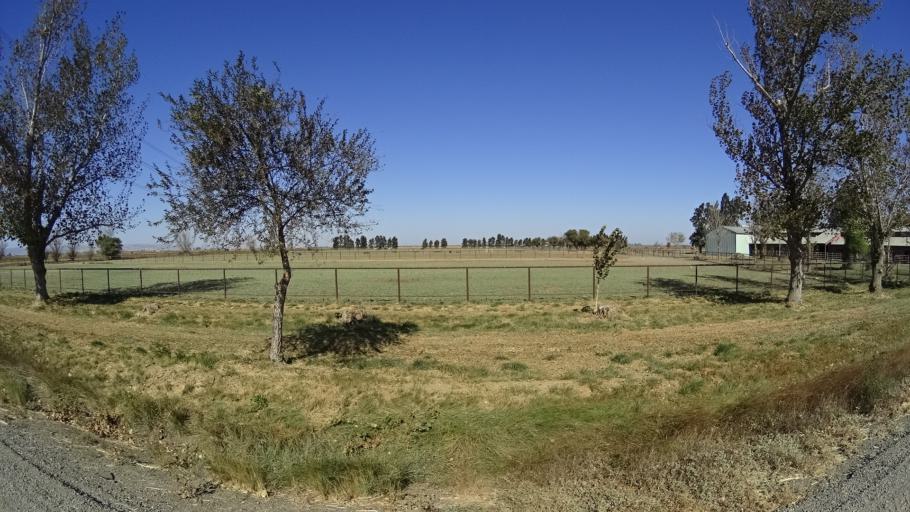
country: US
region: California
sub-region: Yolo County
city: Cottonwood
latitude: 38.6202
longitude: -121.9233
